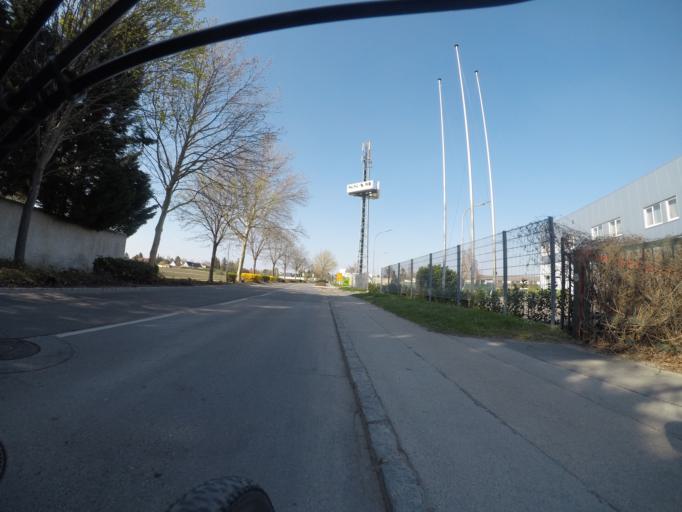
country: AT
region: Lower Austria
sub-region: Politischer Bezirk Modling
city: Neu-Guntramsdorf
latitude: 48.0600
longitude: 16.3234
